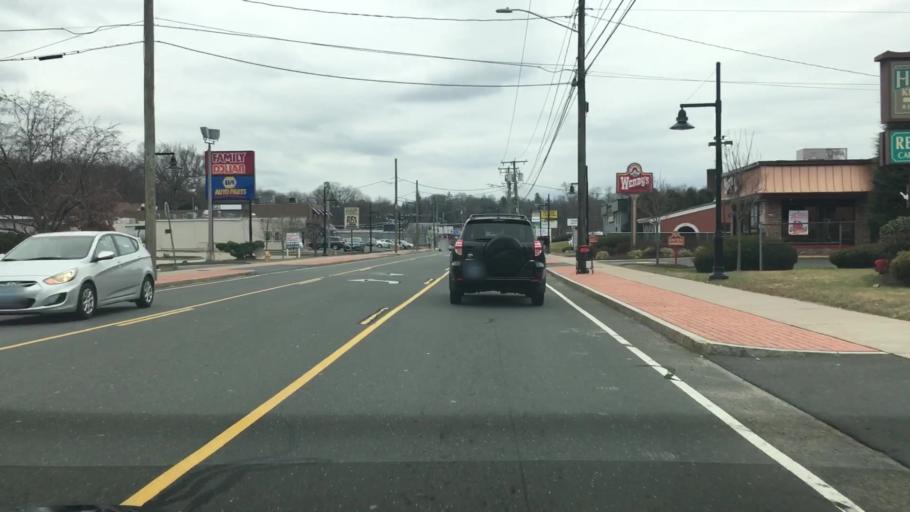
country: US
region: Connecticut
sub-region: Hartford County
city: Manchester
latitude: 41.7807
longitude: -72.5348
